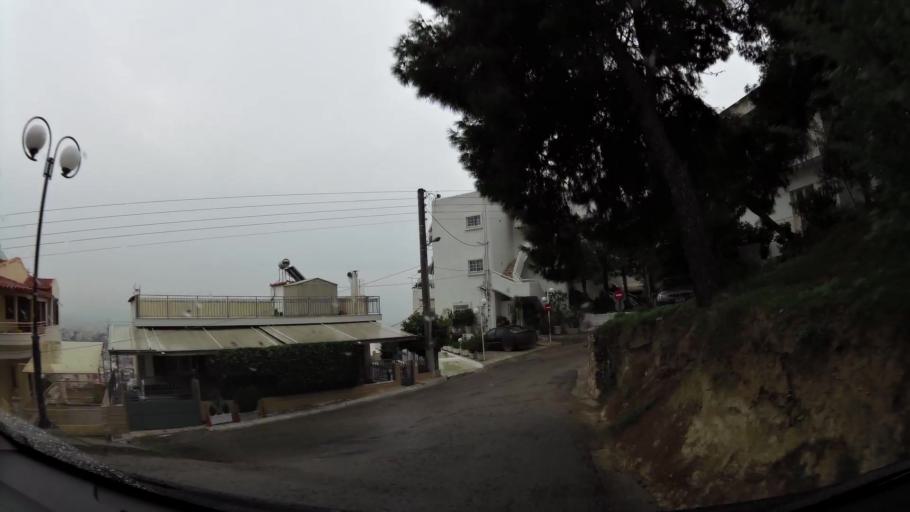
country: GR
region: Attica
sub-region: Nomarchia Athinas
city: Chaidari
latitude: 38.0074
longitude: 23.6575
